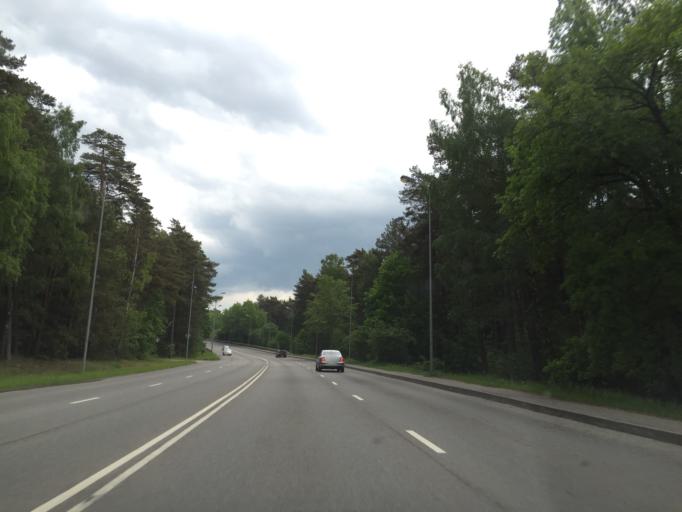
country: LT
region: Klaipedos apskritis
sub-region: Klaipeda
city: Klaipeda
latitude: 55.7355
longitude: 21.1002
